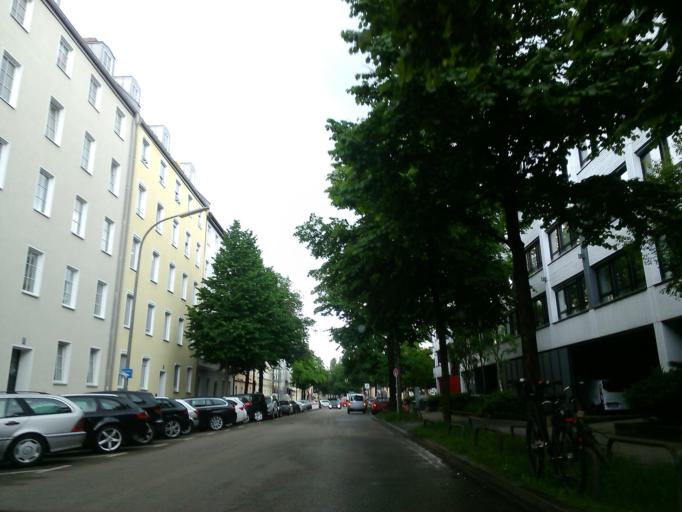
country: DE
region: Bavaria
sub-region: Upper Bavaria
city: Munich
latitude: 48.1275
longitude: 11.5913
